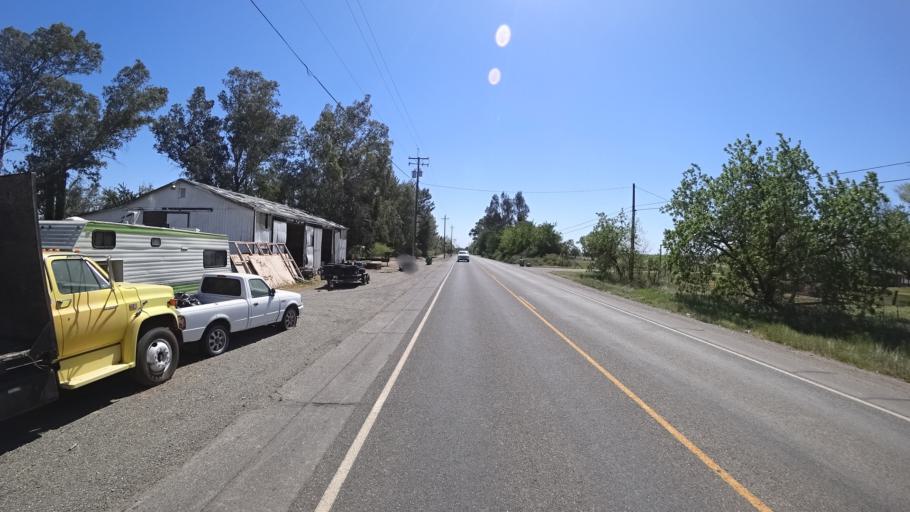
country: US
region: California
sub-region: Glenn County
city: Orland
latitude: 39.7795
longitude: -122.1974
